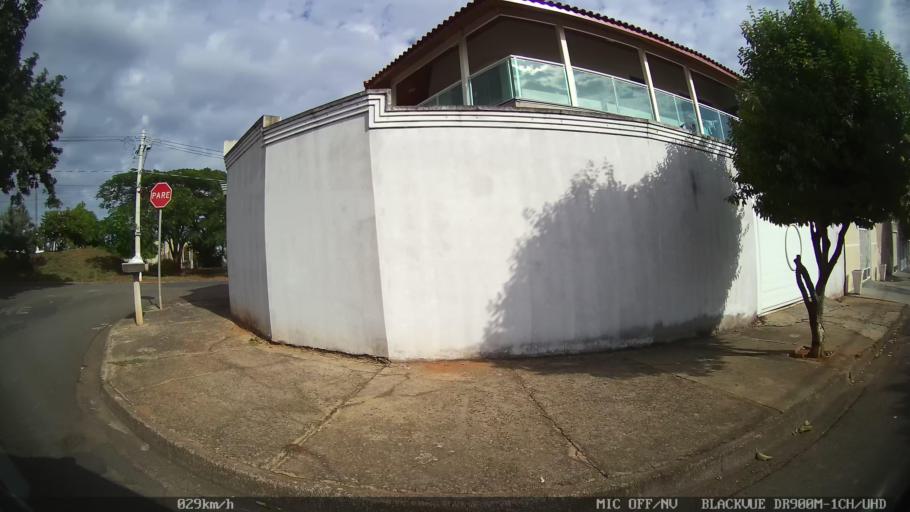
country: BR
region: Sao Paulo
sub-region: Americana
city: Americana
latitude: -22.7198
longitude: -47.3659
